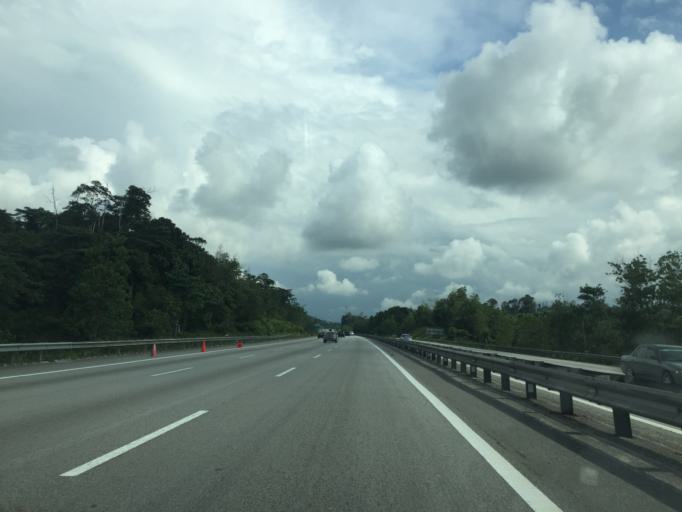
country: MY
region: Selangor
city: Batang Berjuntai
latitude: 3.5623
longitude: 101.5209
